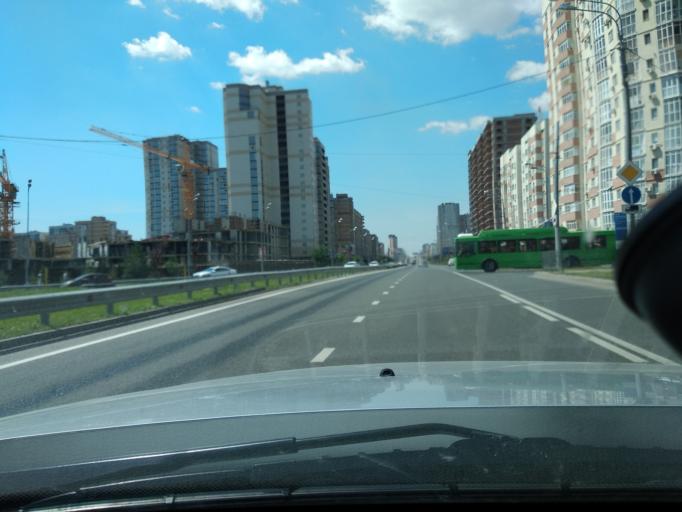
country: RU
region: Tatarstan
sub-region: Gorod Kazan'
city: Kazan
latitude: 55.8194
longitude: 49.1480
